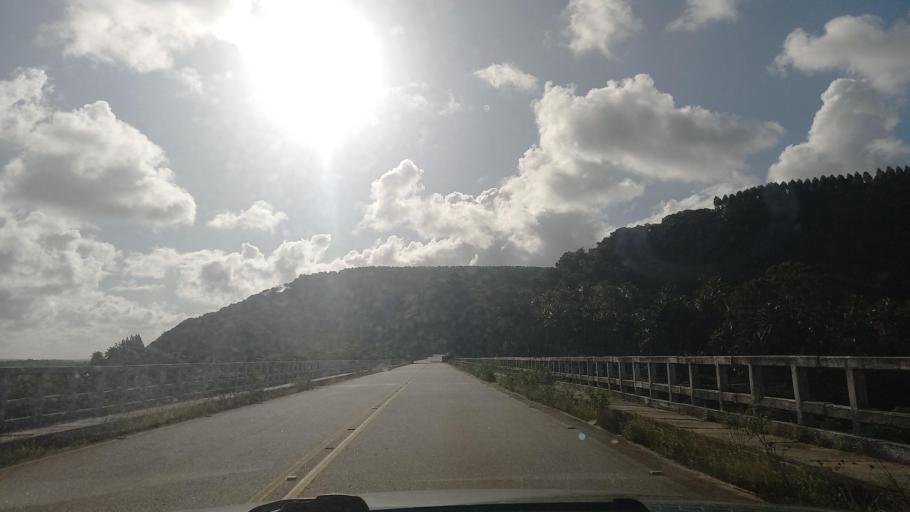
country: BR
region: Alagoas
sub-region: Marechal Deodoro
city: Marechal Deodoro
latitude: -9.8379
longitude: -35.9266
